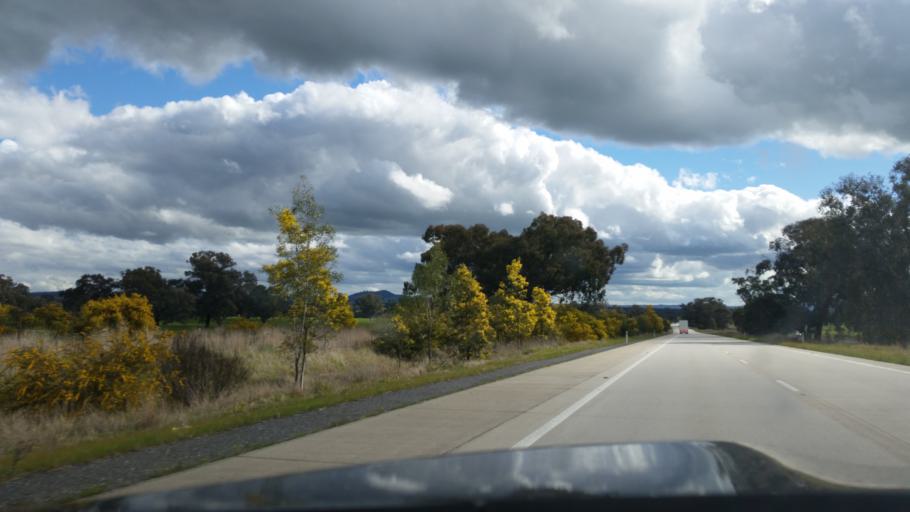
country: AU
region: New South Wales
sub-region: Greater Hume Shire
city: Jindera
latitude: -35.9246
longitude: 147.0468
